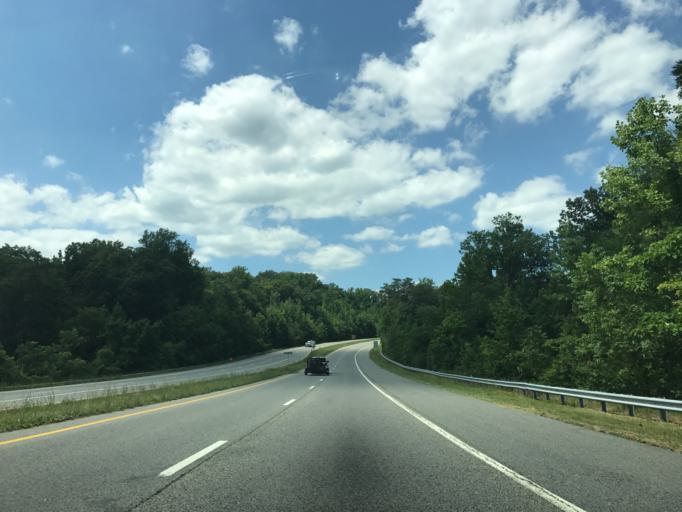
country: US
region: Maryland
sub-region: Prince George's County
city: Glenn Dale
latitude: 39.0030
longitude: -76.7606
